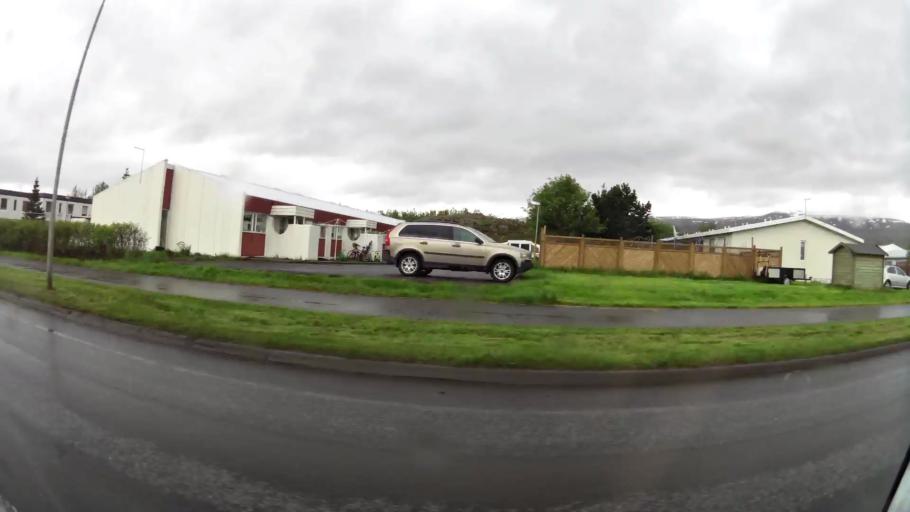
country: IS
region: Northeast
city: Akureyri
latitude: 65.6962
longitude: -18.1135
